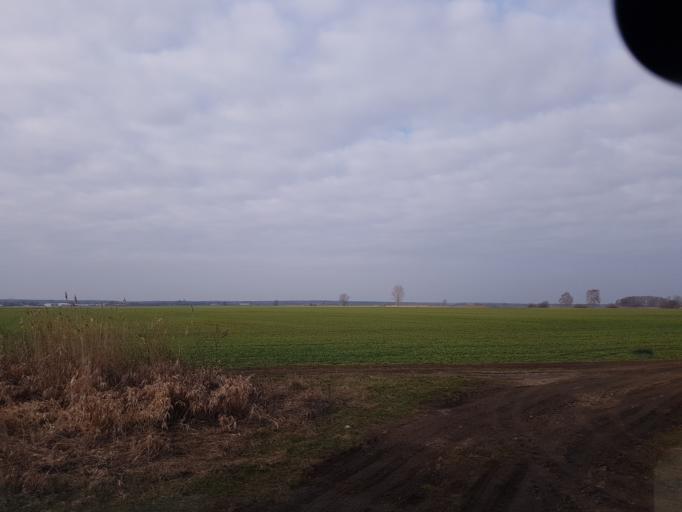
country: DE
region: Brandenburg
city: Doberlug-Kirchhain
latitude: 51.6635
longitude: 13.5658
